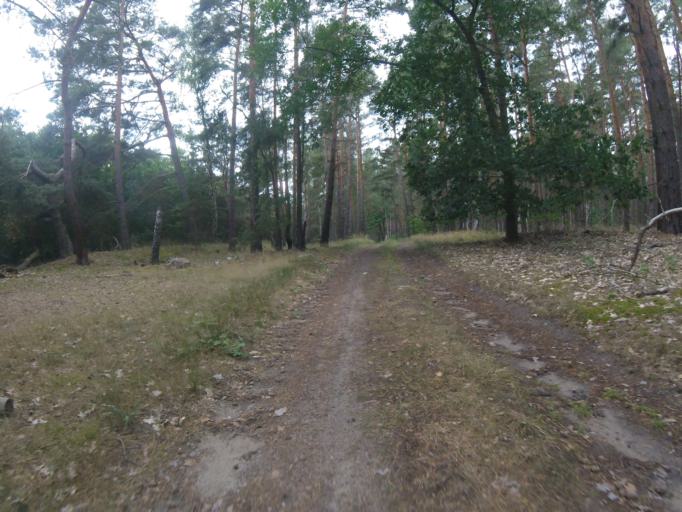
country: DE
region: Brandenburg
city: Bestensee
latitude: 52.2752
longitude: 13.7256
